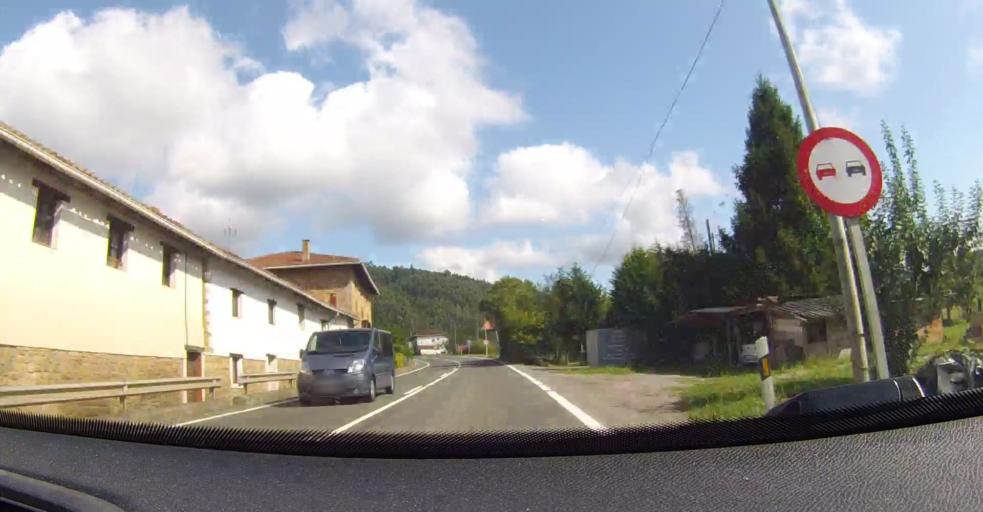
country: ES
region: Basque Country
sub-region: Bizkaia
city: Muxika
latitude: 43.2830
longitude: -2.6878
